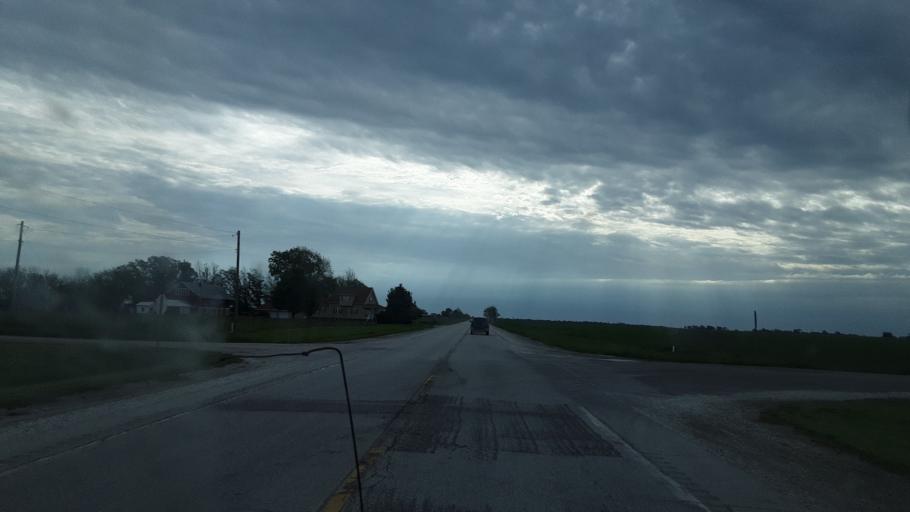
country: US
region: Illinois
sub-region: Hancock County
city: Carthage
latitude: 40.4017
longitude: -91.1986
